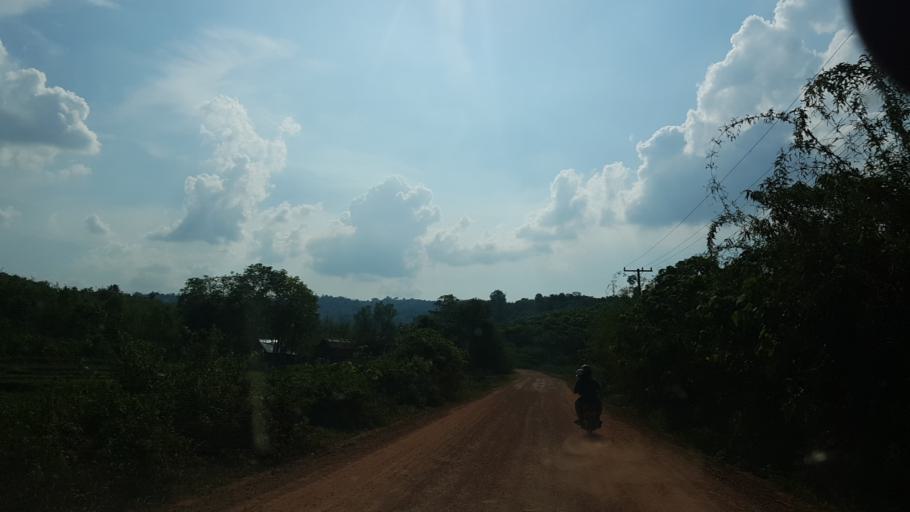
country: LA
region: Vientiane
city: Muang Phon-Hong
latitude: 18.3518
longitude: 102.2800
